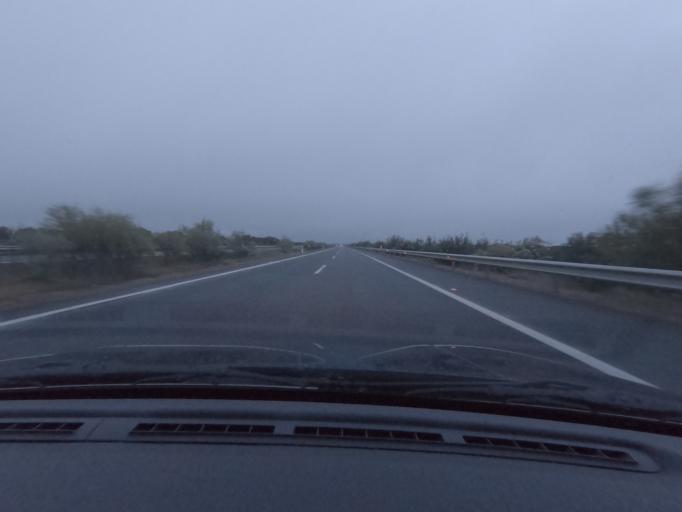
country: ES
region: Extremadura
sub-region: Provincia de Badajoz
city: Carmonita
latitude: 39.1103
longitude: -6.2807
